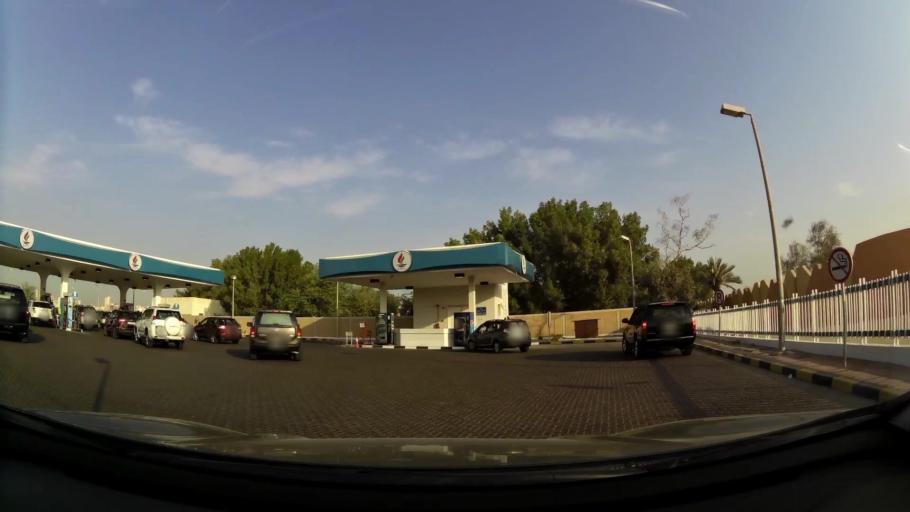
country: KW
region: Muhafazat Hawalli
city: Ar Rumaythiyah
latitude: 29.3166
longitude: 48.0740
